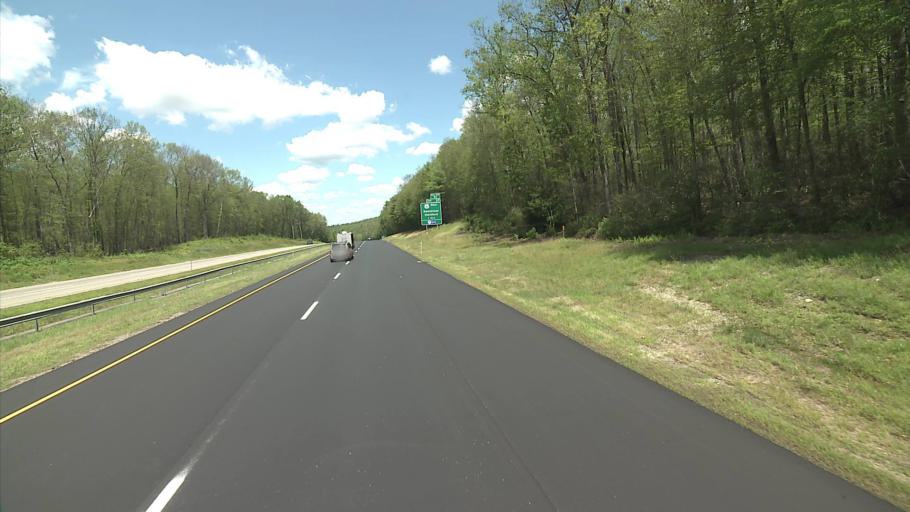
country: US
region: Connecticut
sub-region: Windham County
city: Danielson
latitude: 41.7779
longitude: -71.8718
